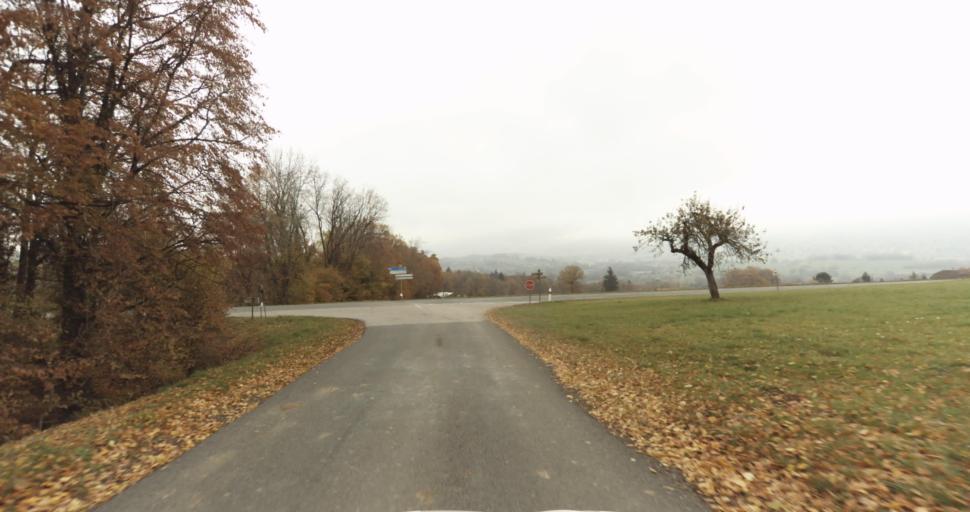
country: FR
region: Rhone-Alpes
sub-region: Departement de la Haute-Savoie
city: Cusy
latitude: 45.7855
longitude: 6.0136
